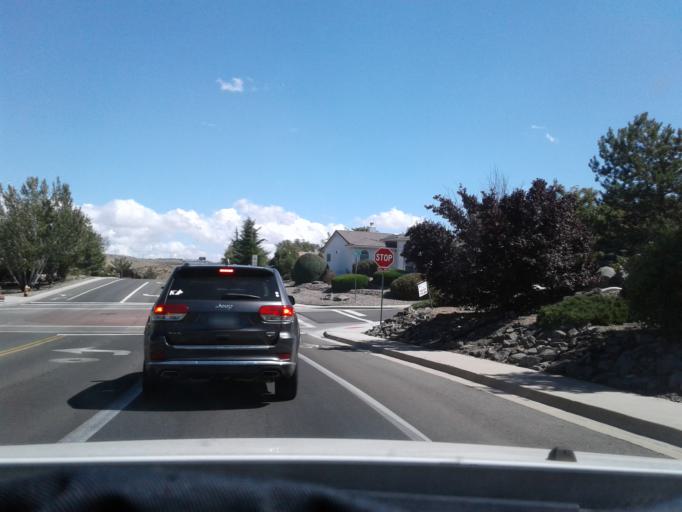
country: US
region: Arizona
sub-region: Yavapai County
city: Prescott
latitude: 34.5732
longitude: -112.4423
